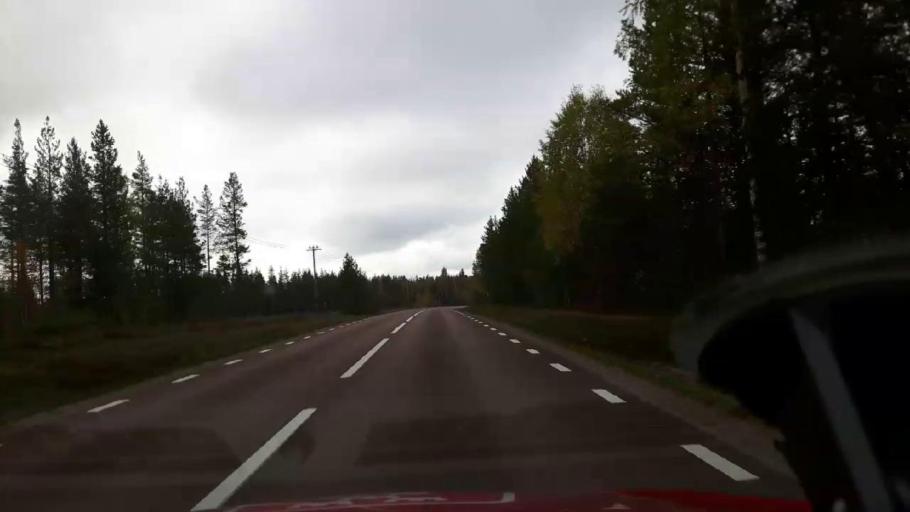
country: SE
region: Jaemtland
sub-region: Harjedalens Kommun
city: Sveg
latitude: 62.2253
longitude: 14.8472
